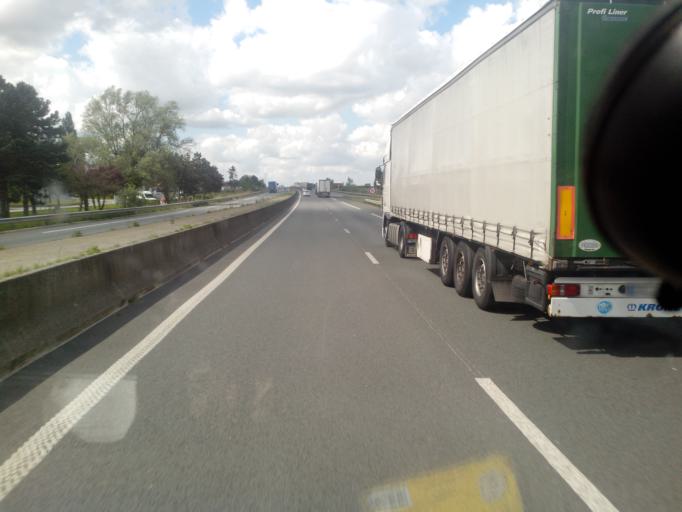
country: FR
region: Nord-Pas-de-Calais
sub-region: Departement du Nord
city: Steenvoorde
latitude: 50.8284
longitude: 2.5829
